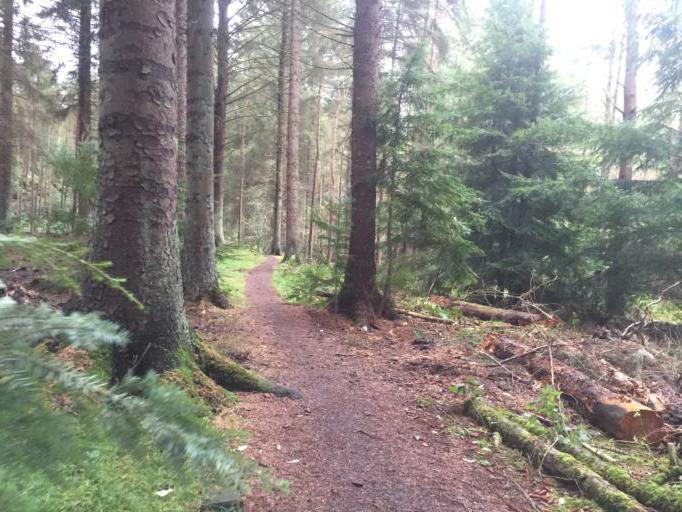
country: GB
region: Scotland
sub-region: West Lothian
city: Linlithgow
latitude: 55.9486
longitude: -3.5895
